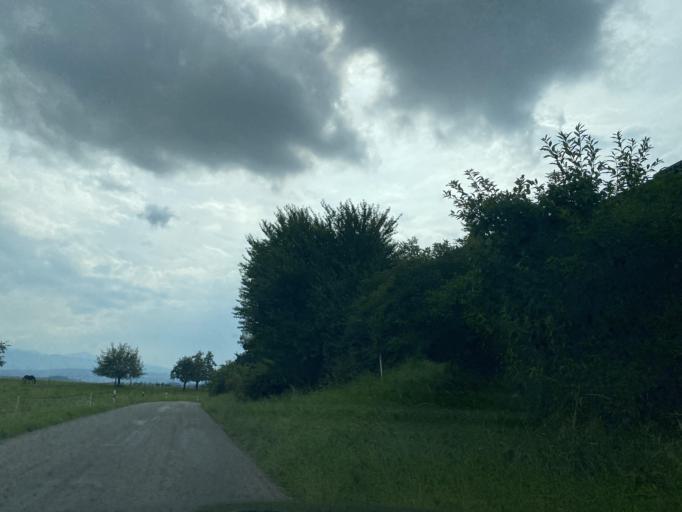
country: CH
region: Zurich
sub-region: Bezirk Hinwil
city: Wetzikon / Kempten
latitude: 47.3350
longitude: 8.8310
